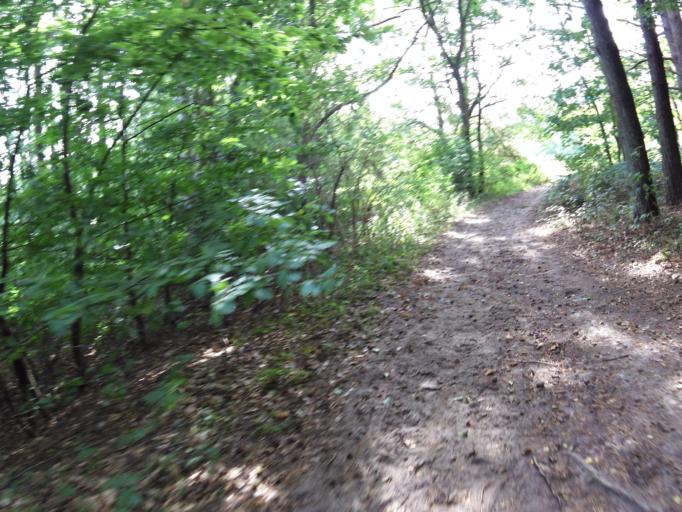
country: DE
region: Mecklenburg-Vorpommern
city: Seebad Bansin
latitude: 53.9510
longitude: 14.1084
